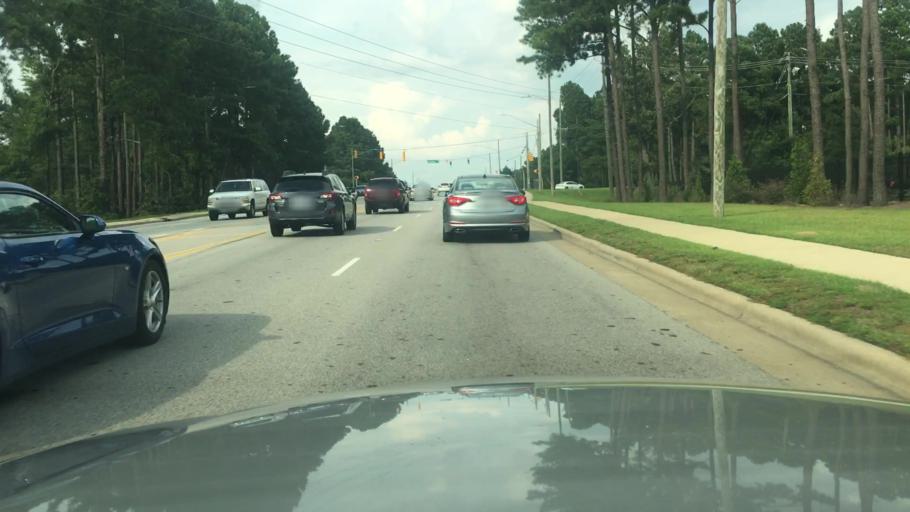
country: US
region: North Carolina
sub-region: Cumberland County
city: Fort Bragg
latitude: 35.0963
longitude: -78.9711
